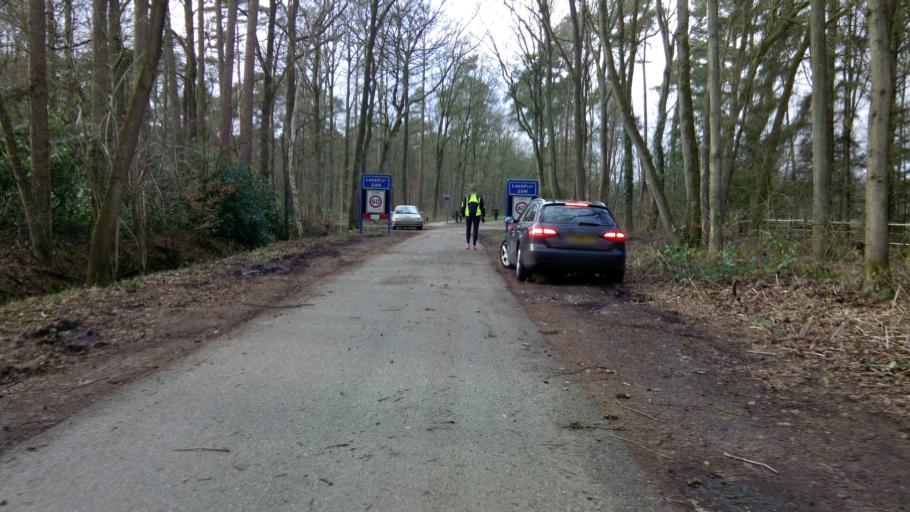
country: NL
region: Utrecht
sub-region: Gemeente Amersfoort
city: Randenbroek
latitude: 52.1206
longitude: 5.3955
